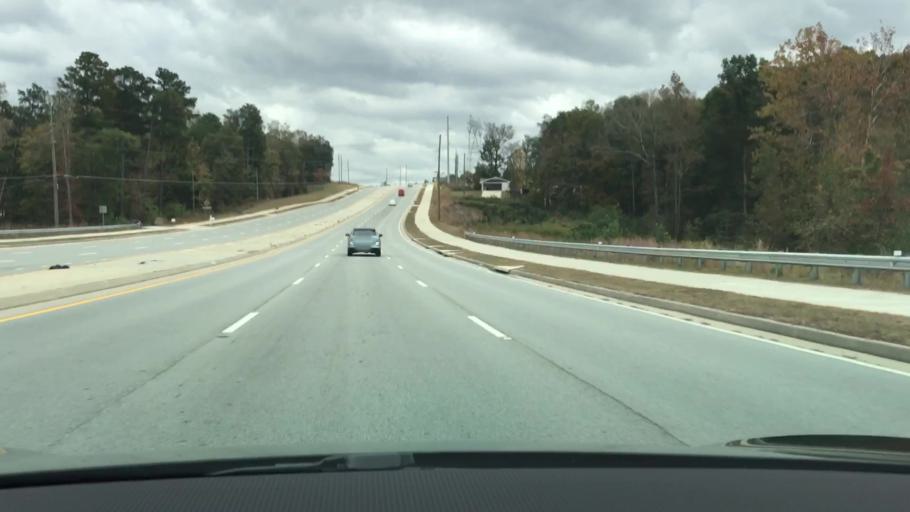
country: US
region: Georgia
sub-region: Hall County
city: Flowery Branch
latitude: 34.1122
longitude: -83.8935
